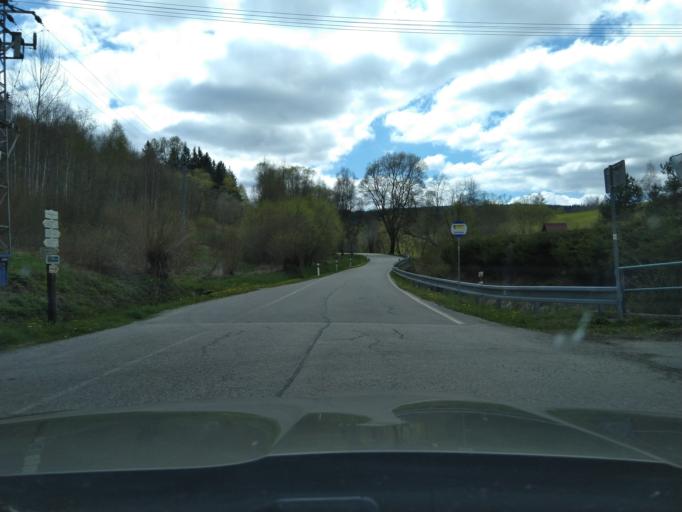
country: CZ
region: Jihocesky
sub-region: Okres Prachatice
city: Vimperk
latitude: 49.0344
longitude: 13.7587
